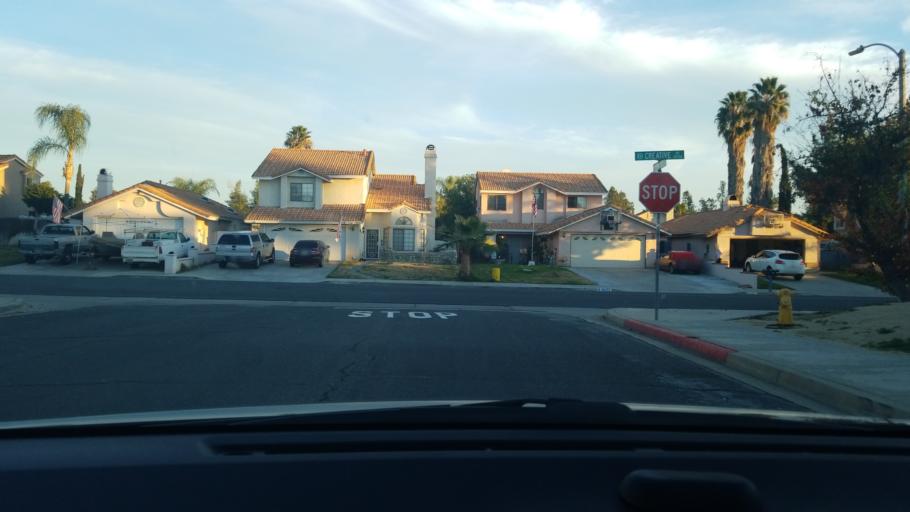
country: US
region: California
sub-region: Riverside County
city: Murrieta Hot Springs
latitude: 33.5422
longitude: -117.1489
